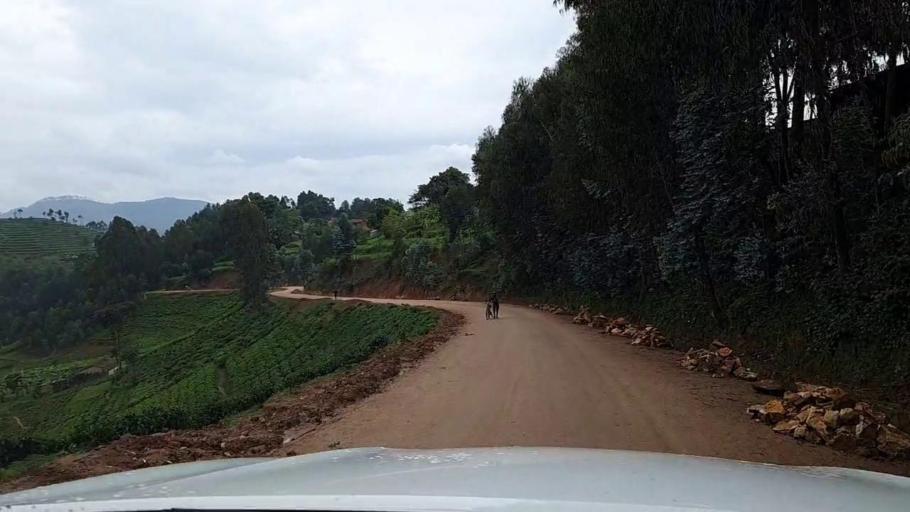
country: RW
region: Southern Province
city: Nzega
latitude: -2.4608
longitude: 29.4663
